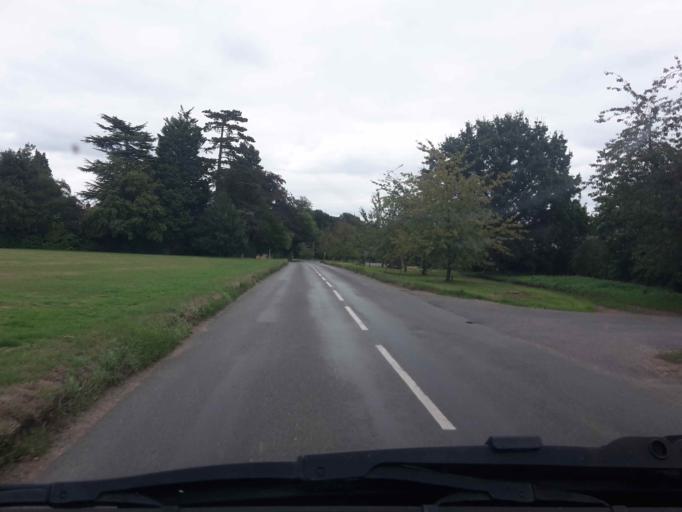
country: GB
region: England
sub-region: Oxfordshire
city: Rotherfield Peppard
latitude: 51.5411
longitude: -0.9639
